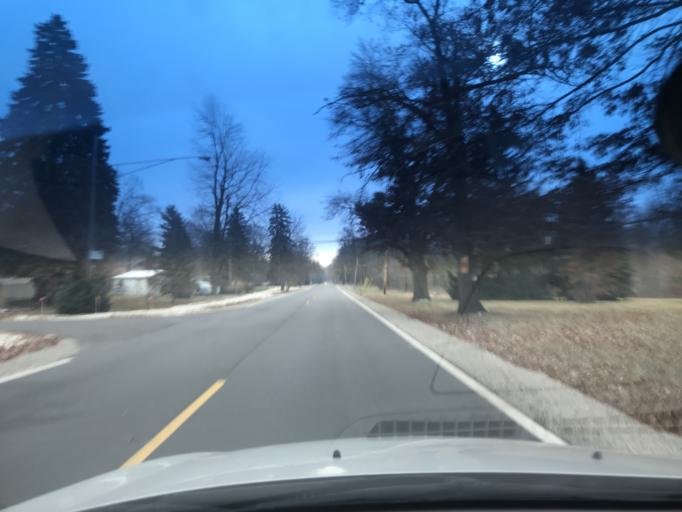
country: US
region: Michigan
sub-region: Macomb County
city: Shelby
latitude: 42.6643
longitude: -83.0598
